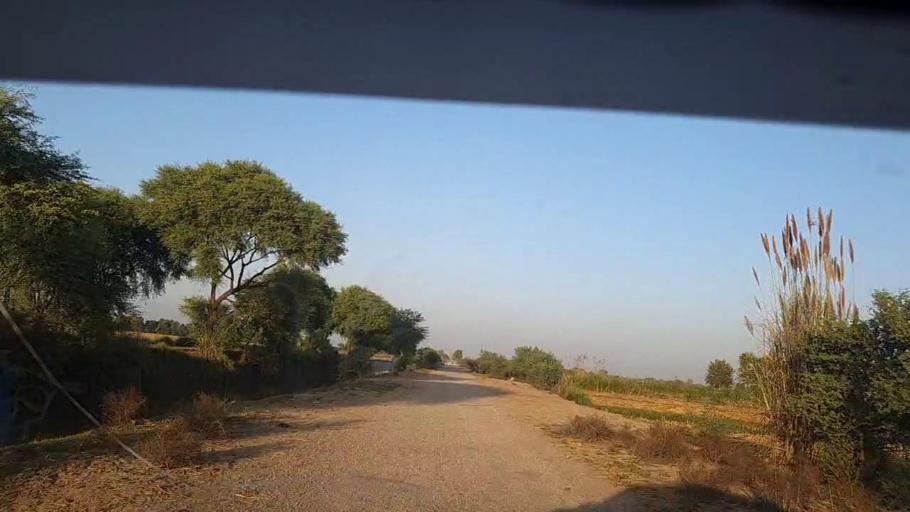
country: PK
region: Sindh
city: Ratodero
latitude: 27.8839
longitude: 68.2103
